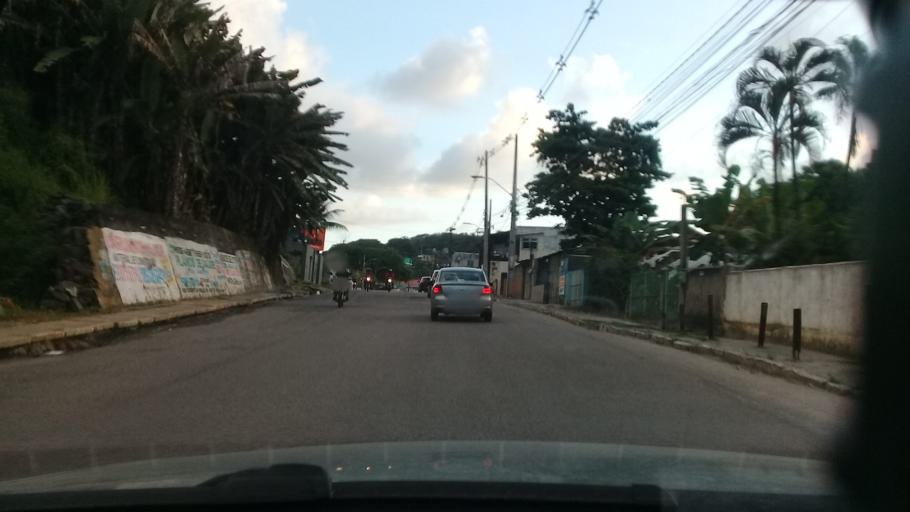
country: BR
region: Pernambuco
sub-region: Jaboatao Dos Guararapes
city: Jaboatao dos Guararapes
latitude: -8.1071
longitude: -34.9837
